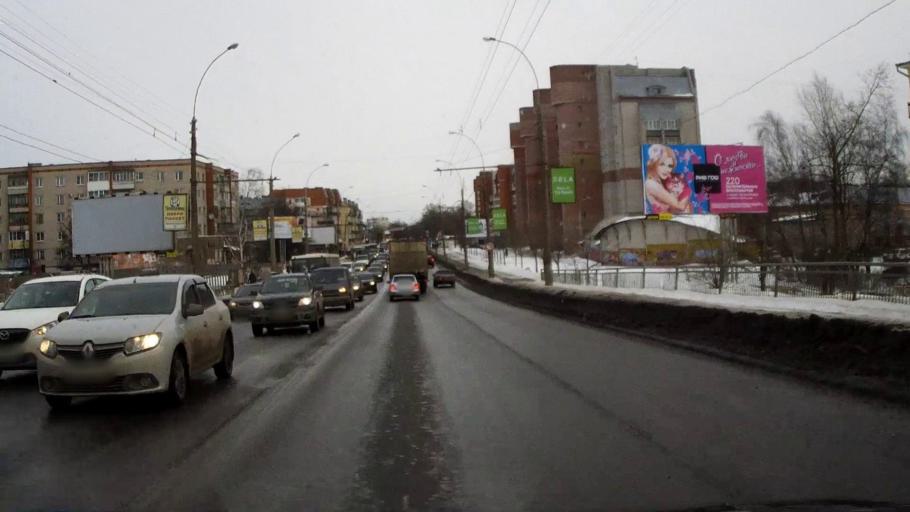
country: RU
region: Vologda
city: Vologda
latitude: 59.2179
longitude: 39.8647
